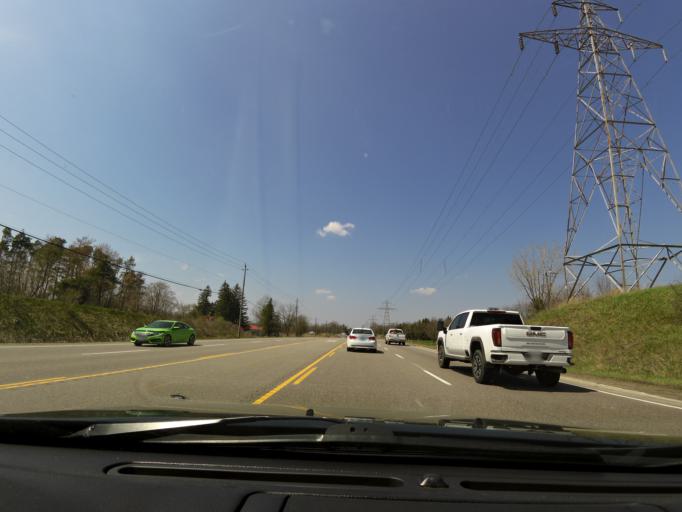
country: CA
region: Ontario
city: Ancaster
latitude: 43.3576
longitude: -79.9797
